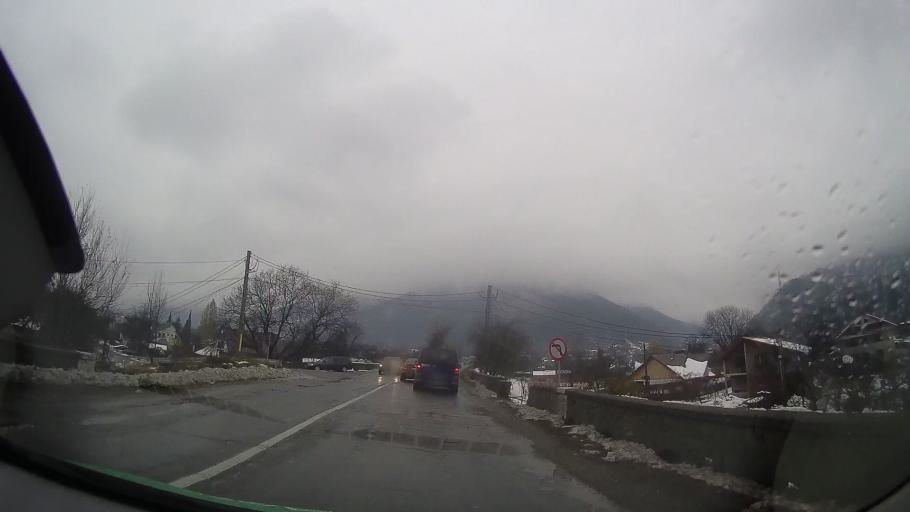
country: RO
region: Neamt
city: Viisoara
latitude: 46.9287
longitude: 26.2255
